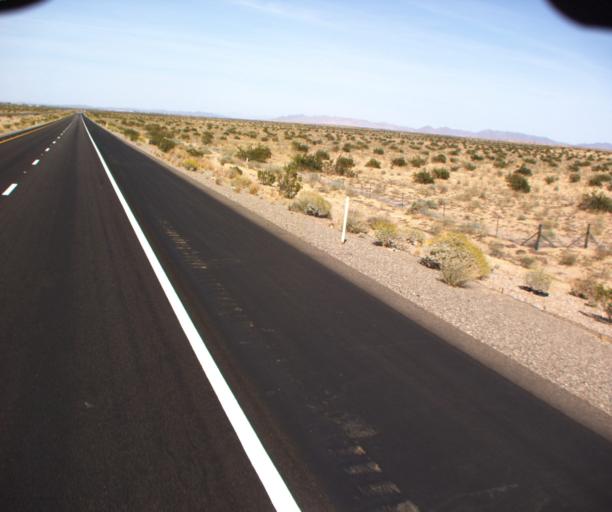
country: US
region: Arizona
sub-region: Yuma County
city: Somerton
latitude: 32.5660
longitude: -114.5587
